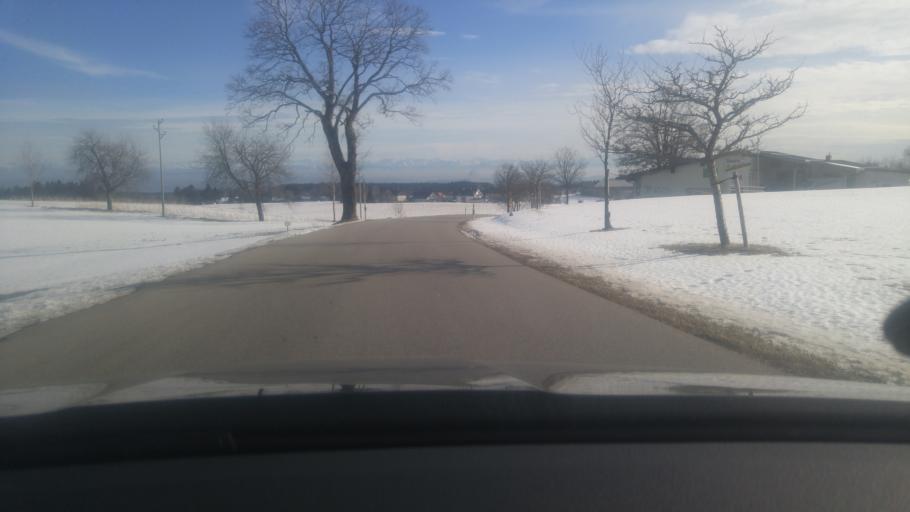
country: DE
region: Baden-Wuerttemberg
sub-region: Freiburg Region
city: Hochenschwand
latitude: 47.7156
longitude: 8.1522
